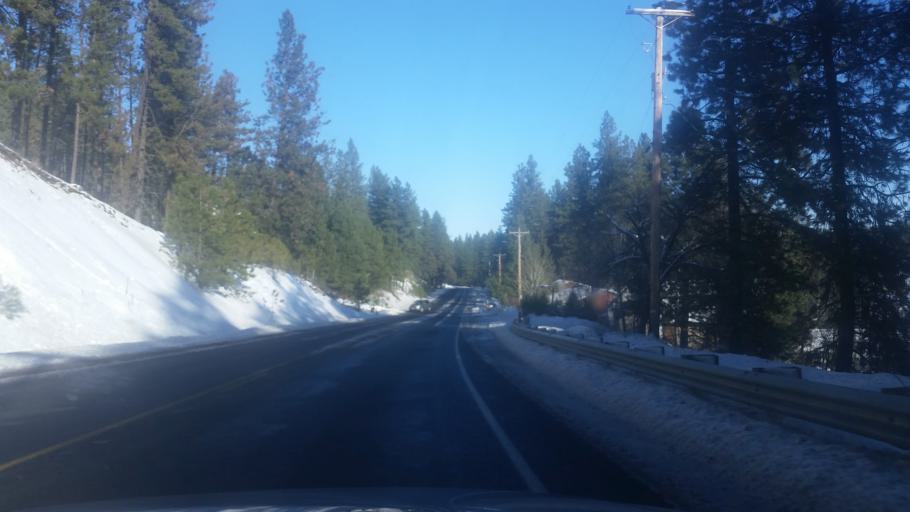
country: US
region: Washington
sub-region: Spokane County
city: Cheney
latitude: 47.5195
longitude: -117.5254
